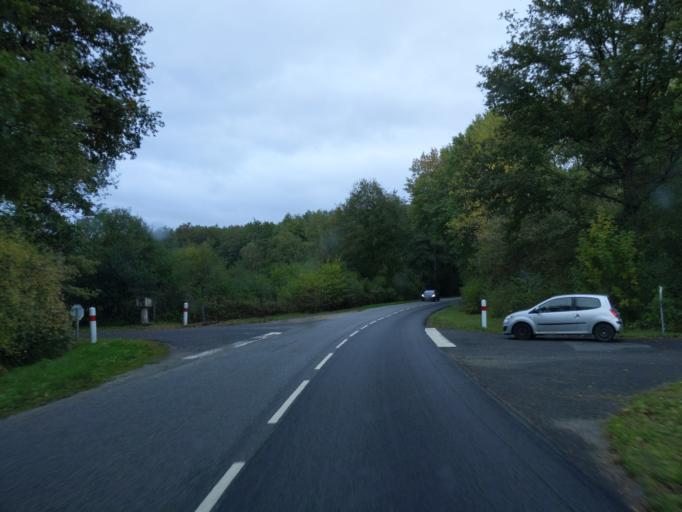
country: FR
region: Ile-de-France
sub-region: Departement des Yvelines
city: Bullion
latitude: 48.6015
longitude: 1.9939
